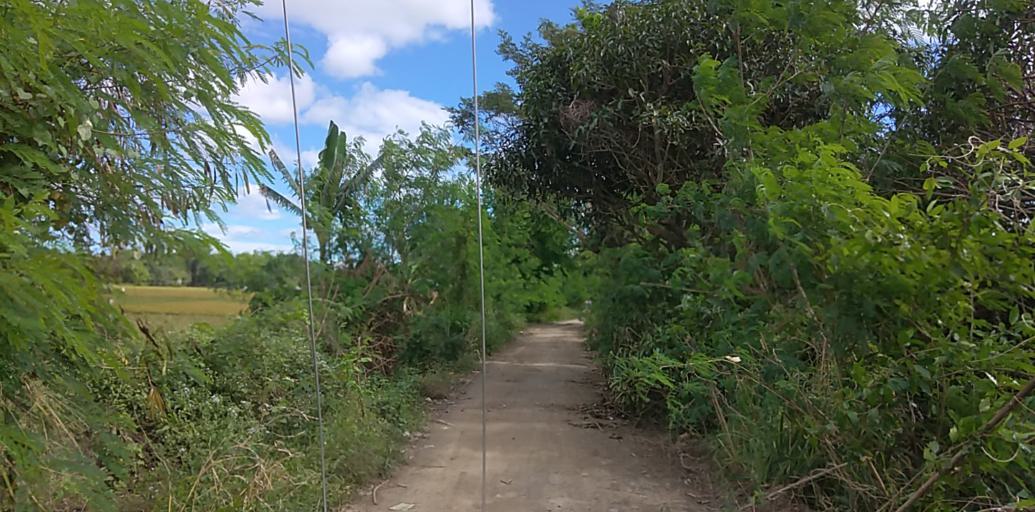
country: PH
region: Central Luzon
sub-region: Province of Pampanga
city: Santa Ana
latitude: 15.1183
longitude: 120.7781
